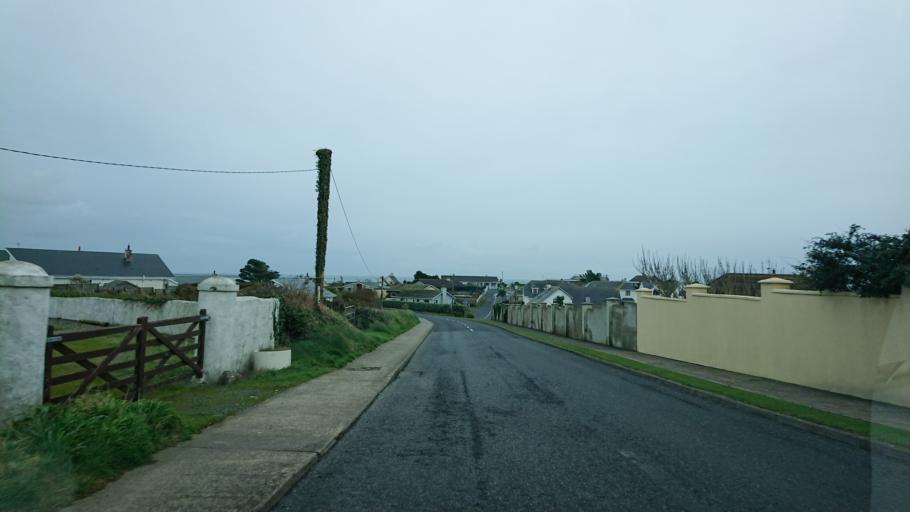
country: IE
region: Munster
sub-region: Waterford
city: Dunmore East
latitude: 52.1470
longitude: -7.0029
